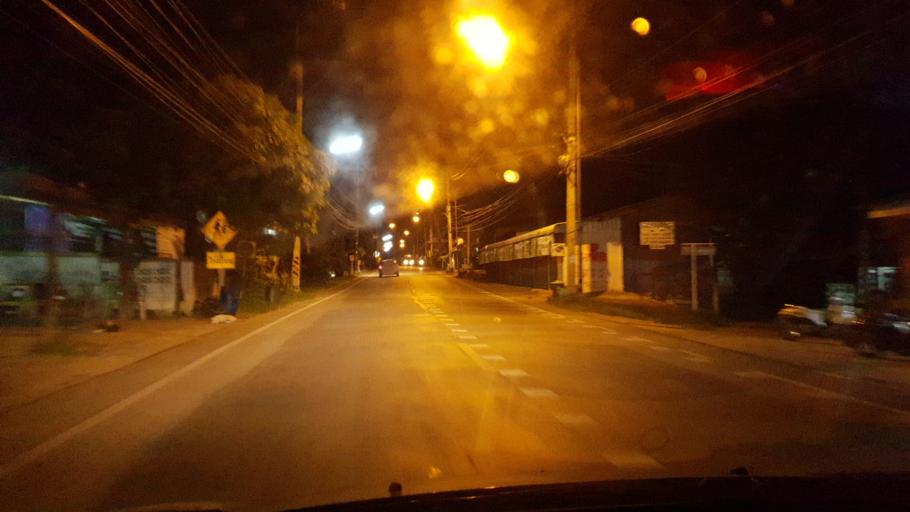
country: TH
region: Mae Hong Son
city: Khun Yuam
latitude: 18.8339
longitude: 97.9374
